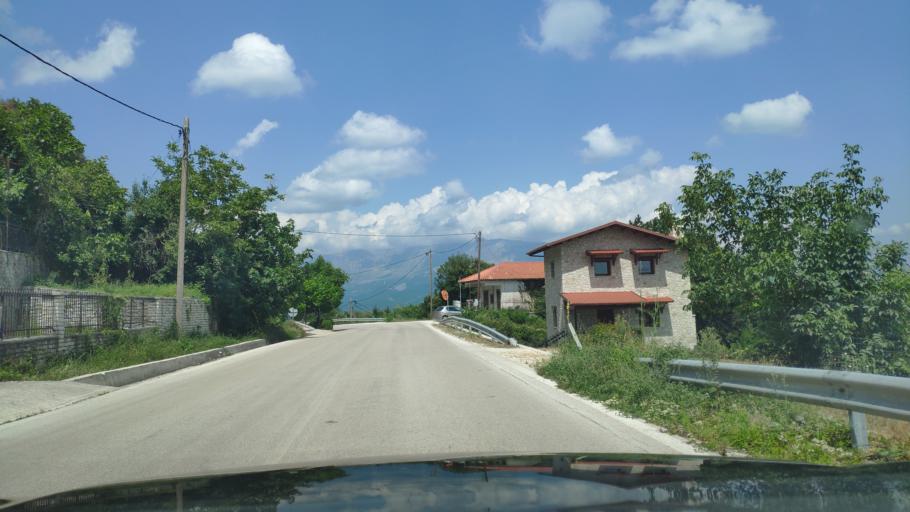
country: GR
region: Epirus
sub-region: Nomos Artas
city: Agios Dimitrios
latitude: 39.3271
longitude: 20.9977
